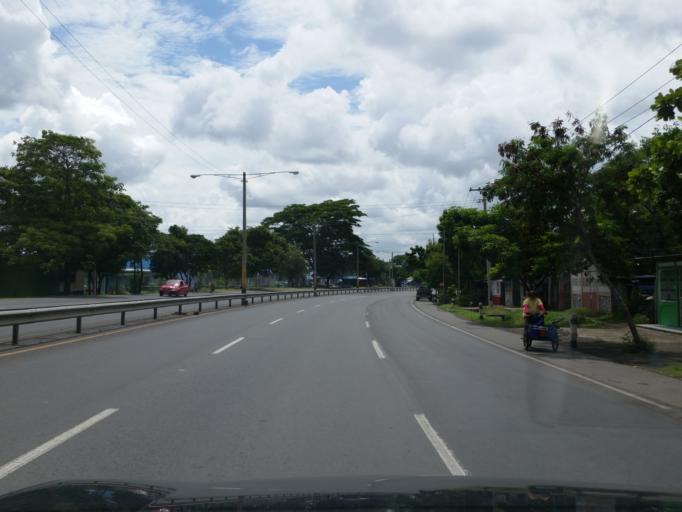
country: NI
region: Managua
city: Managua
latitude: 12.1453
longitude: -86.1660
